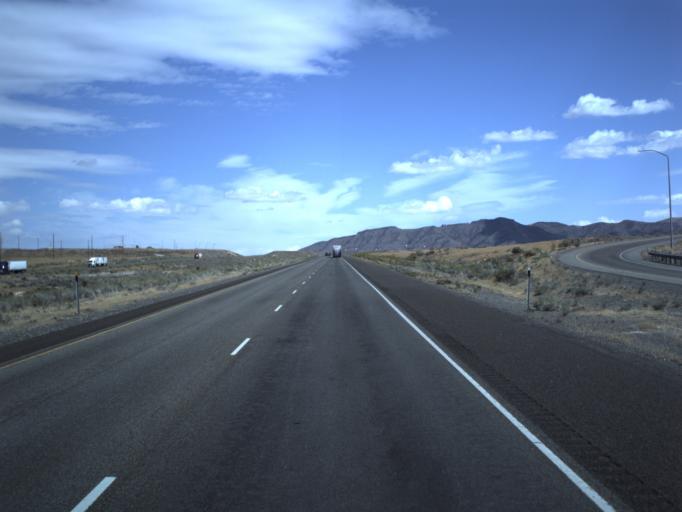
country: US
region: Utah
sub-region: Tooele County
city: Grantsville
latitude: 40.7565
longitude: -113.0227
